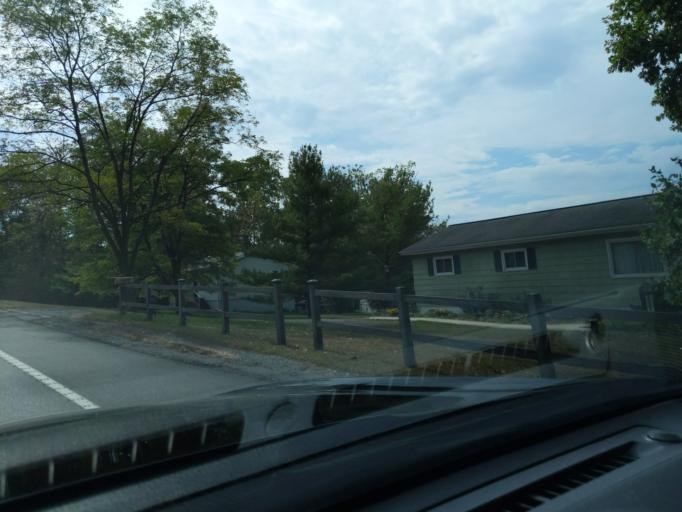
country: US
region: Pennsylvania
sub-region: Blair County
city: Lakemont
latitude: 40.4748
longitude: -78.3893
